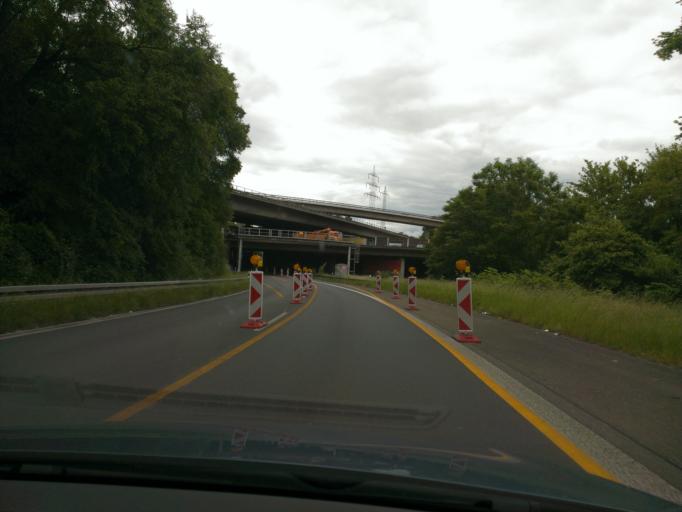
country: DE
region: North Rhine-Westphalia
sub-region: Regierungsbezirk Koln
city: Merheim
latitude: 50.9515
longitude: 7.0351
